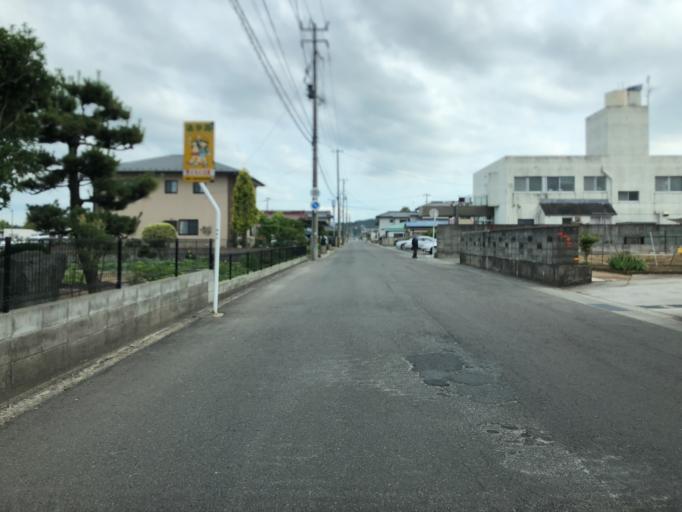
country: JP
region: Fukushima
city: Fukushima-shi
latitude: 37.7406
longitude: 140.4176
